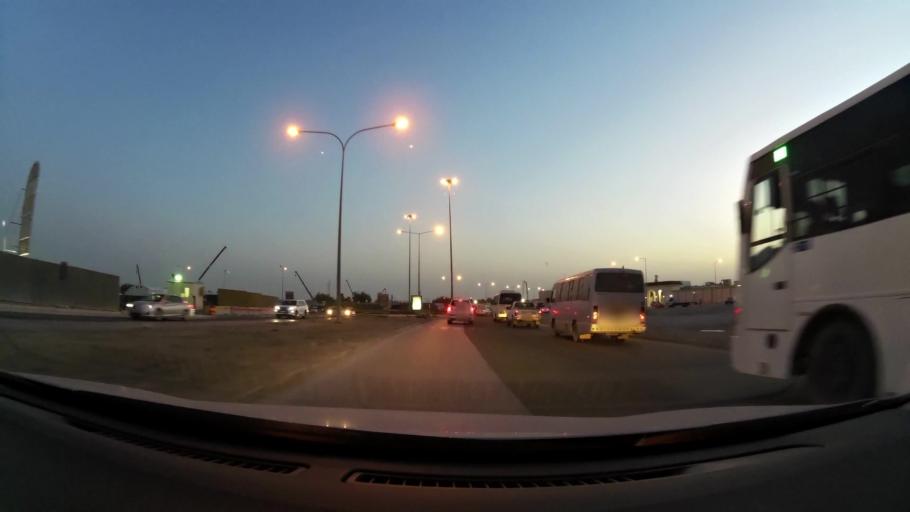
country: QA
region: Baladiyat ar Rayyan
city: Ar Rayyan
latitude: 25.3053
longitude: 51.4540
